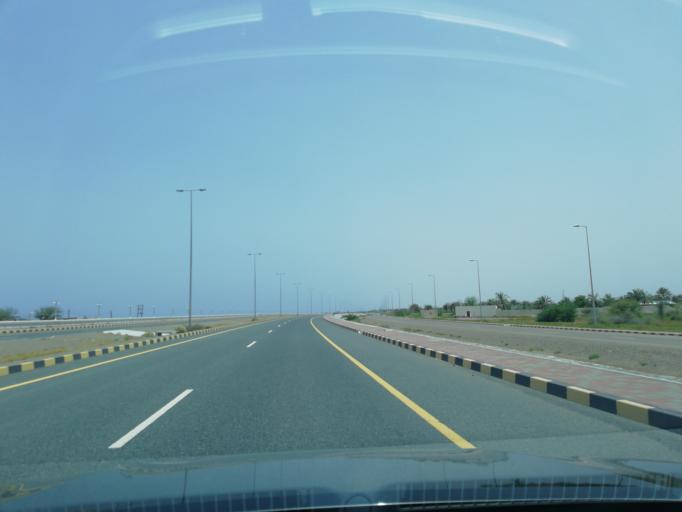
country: OM
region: Al Batinah
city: Shinas
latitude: 24.8261
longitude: 56.4372
